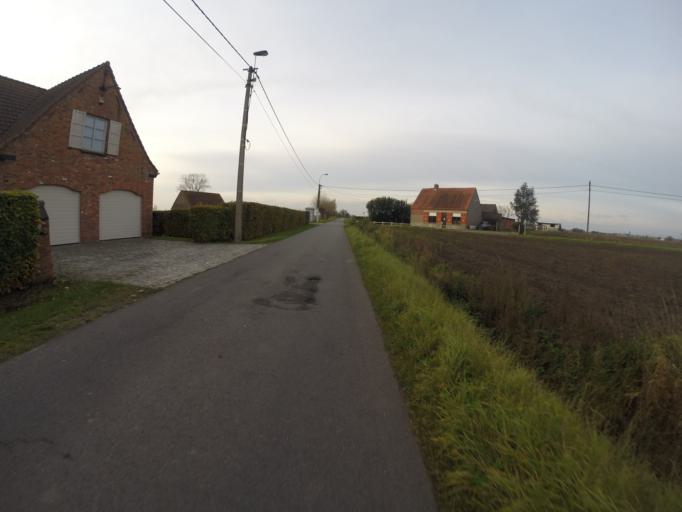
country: BE
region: Flanders
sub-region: Provincie Oost-Vlaanderen
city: Aalter
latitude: 51.0634
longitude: 3.4475
